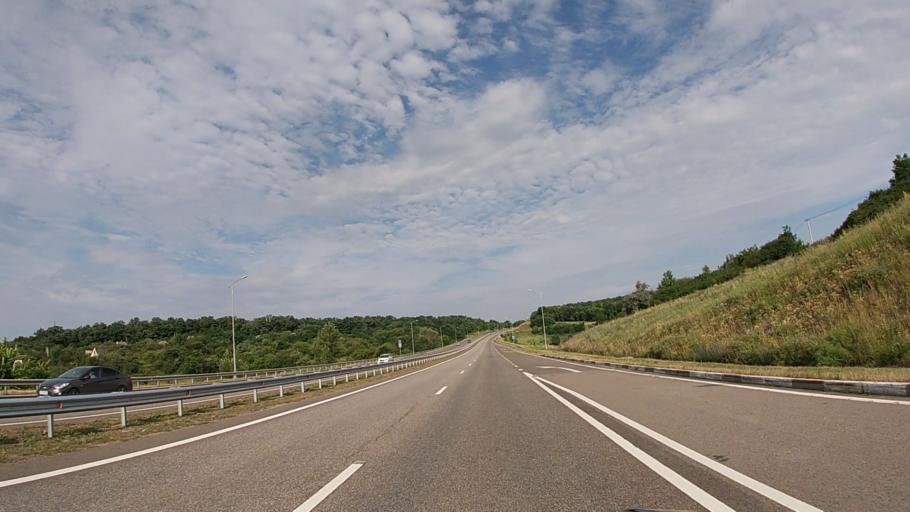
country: RU
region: Belgorod
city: Tomarovka
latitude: 50.6616
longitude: 36.3420
